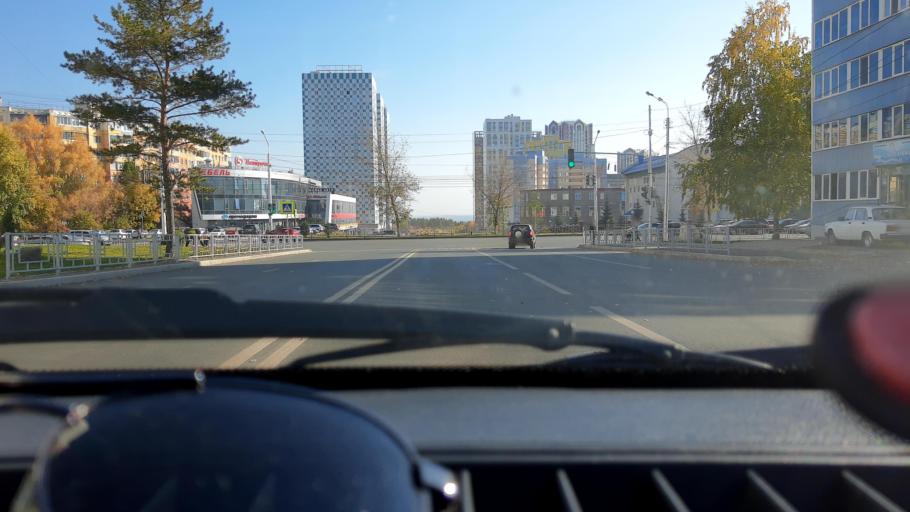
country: RU
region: Bashkortostan
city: Ufa
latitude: 54.7675
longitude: 56.0275
